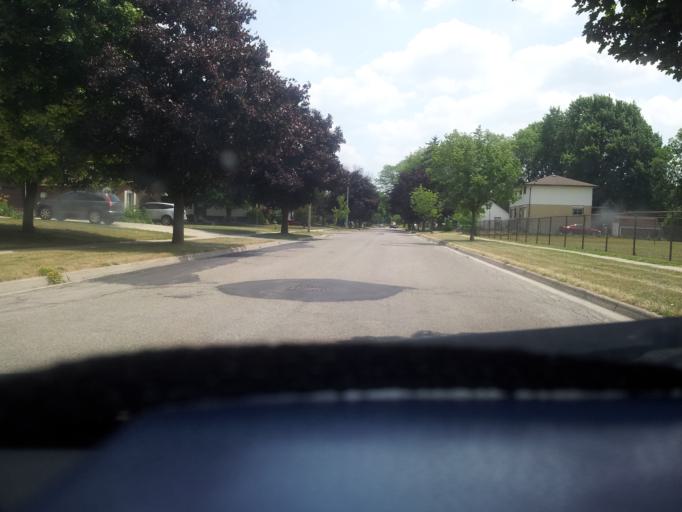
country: CA
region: Ontario
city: Stratford
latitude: 43.3628
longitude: -80.9967
